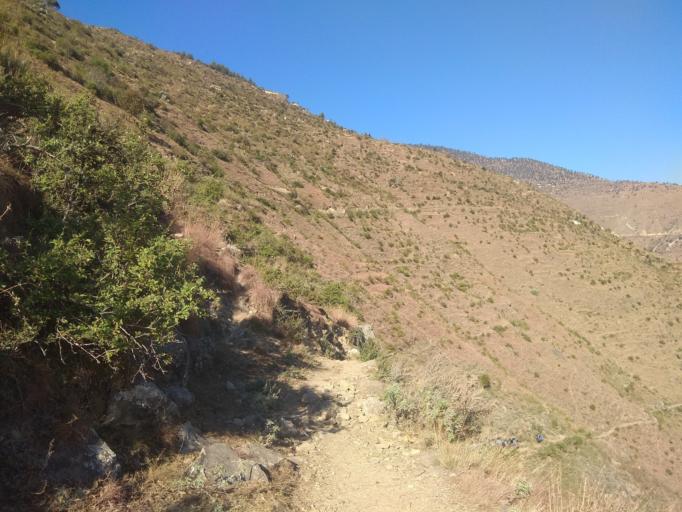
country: NP
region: Mid Western
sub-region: Karnali Zone
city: Jumla
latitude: 29.3136
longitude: 81.7420
